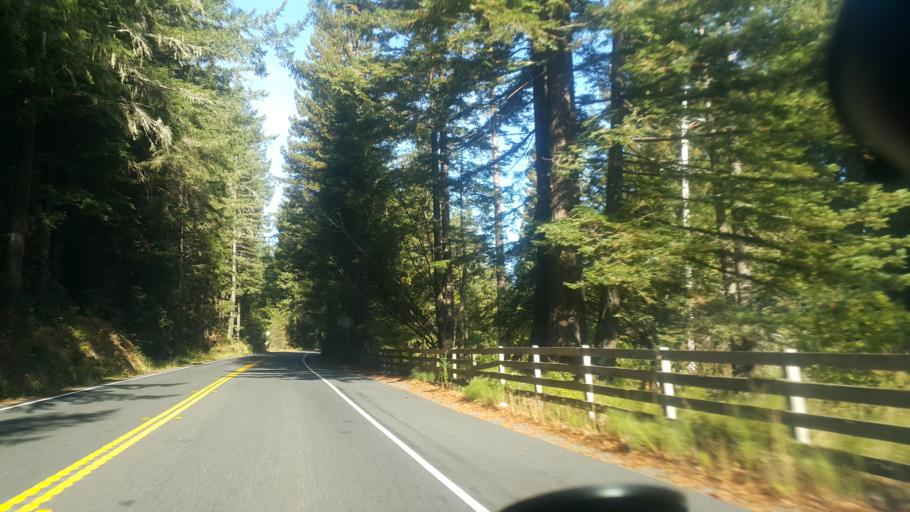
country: US
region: California
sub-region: Mendocino County
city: Fort Bragg
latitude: 39.3505
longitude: -123.6057
